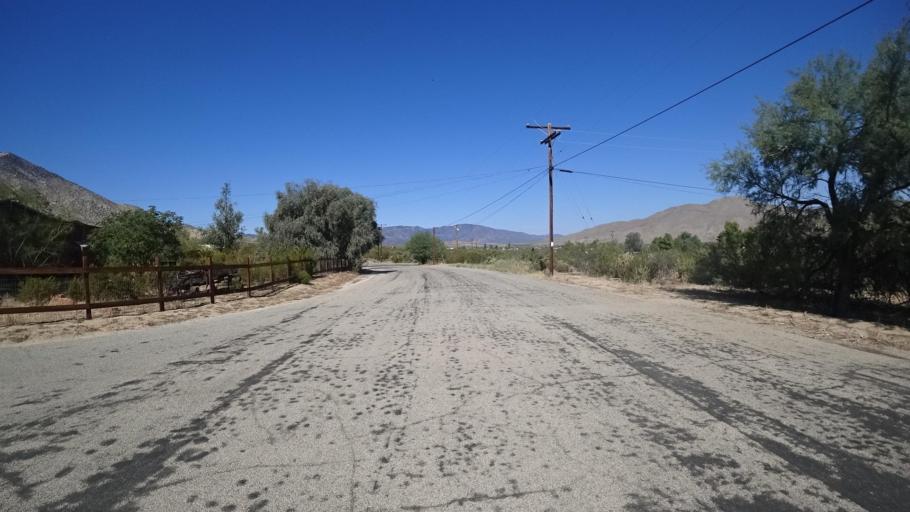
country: US
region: California
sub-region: San Diego County
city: Julian
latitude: 33.0745
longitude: -116.4435
